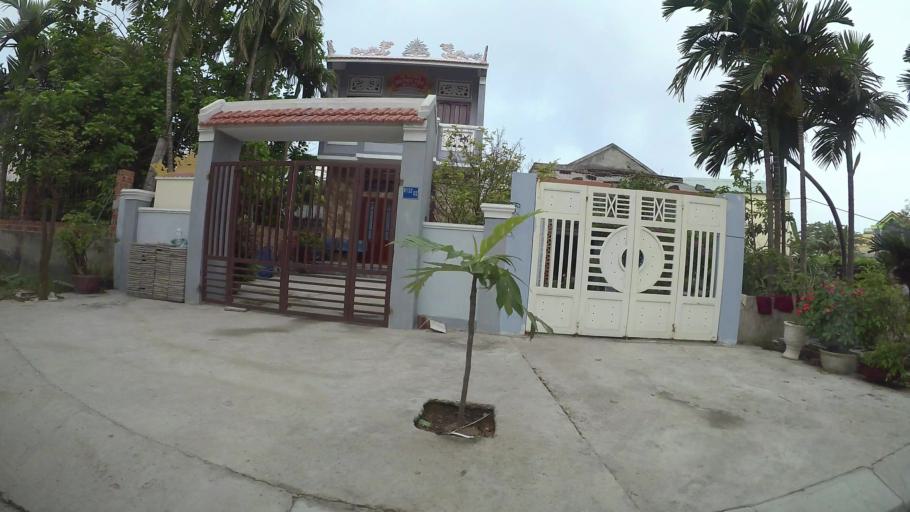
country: VN
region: Da Nang
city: Son Tra
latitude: 16.0845
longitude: 108.2473
